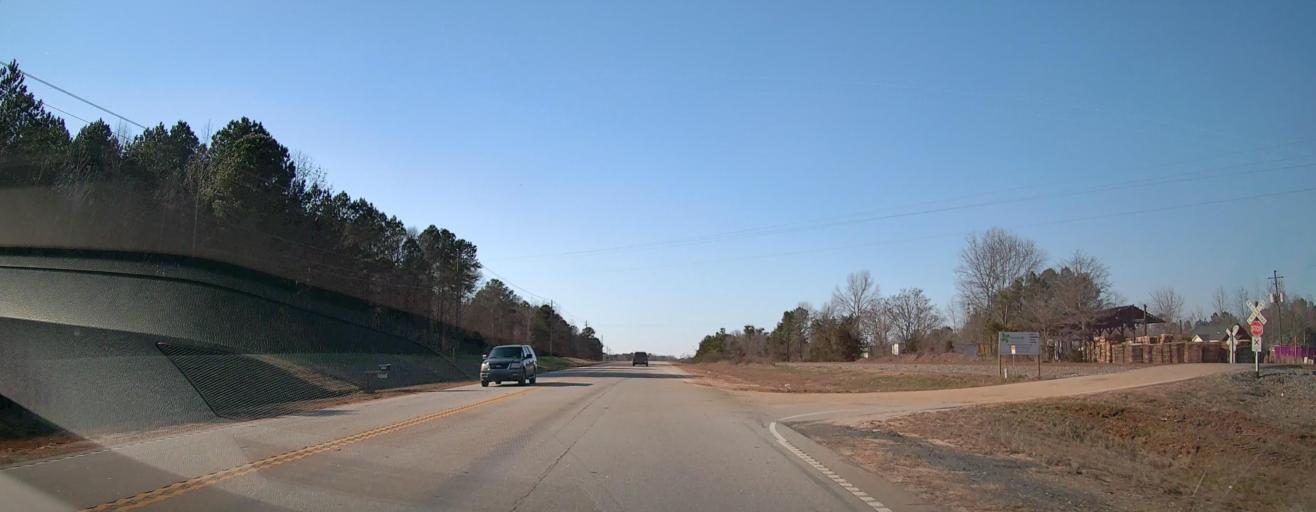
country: US
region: Georgia
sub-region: Butts County
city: Jackson
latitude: 33.3220
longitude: -83.9948
